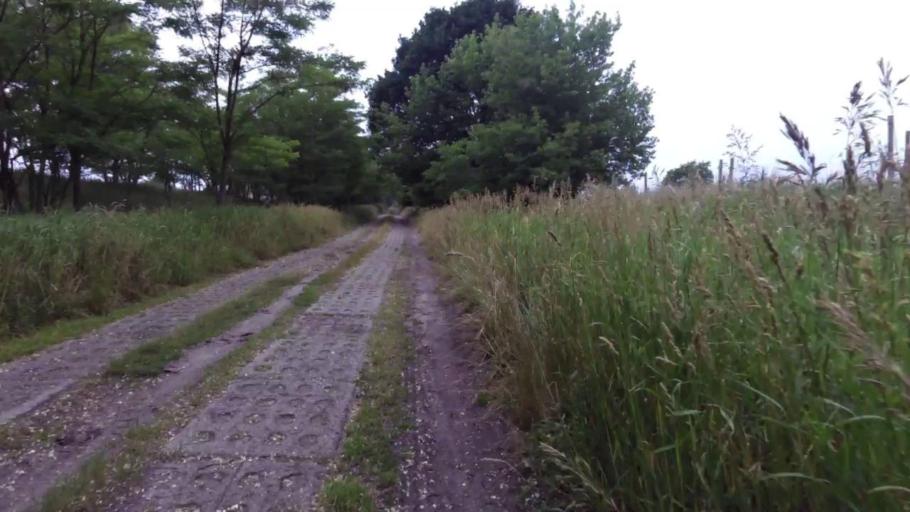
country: PL
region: West Pomeranian Voivodeship
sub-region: Powiat goleniowski
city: Stepnica
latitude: 53.7175
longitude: 14.5658
